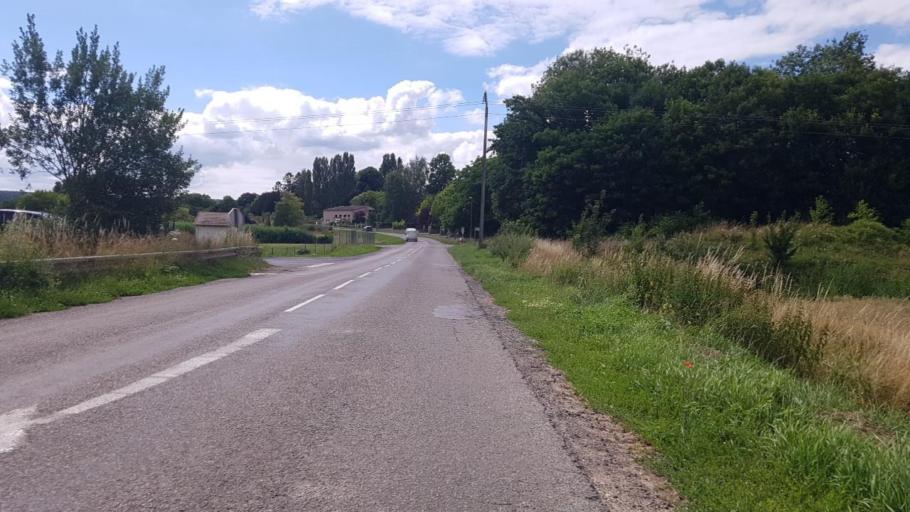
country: FR
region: Champagne-Ardenne
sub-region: Departement de la Marne
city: Dormans
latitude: 49.0780
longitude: 3.6288
